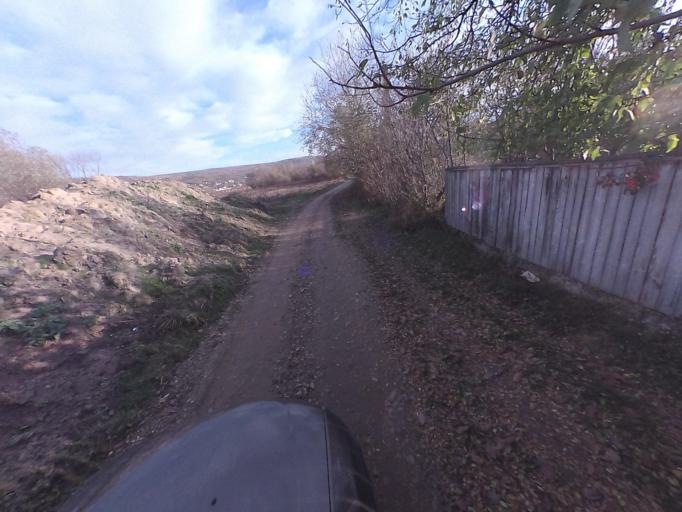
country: RO
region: Vaslui
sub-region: Comuna Gherghesti
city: Gherghesti
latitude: 46.4904
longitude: 27.5283
